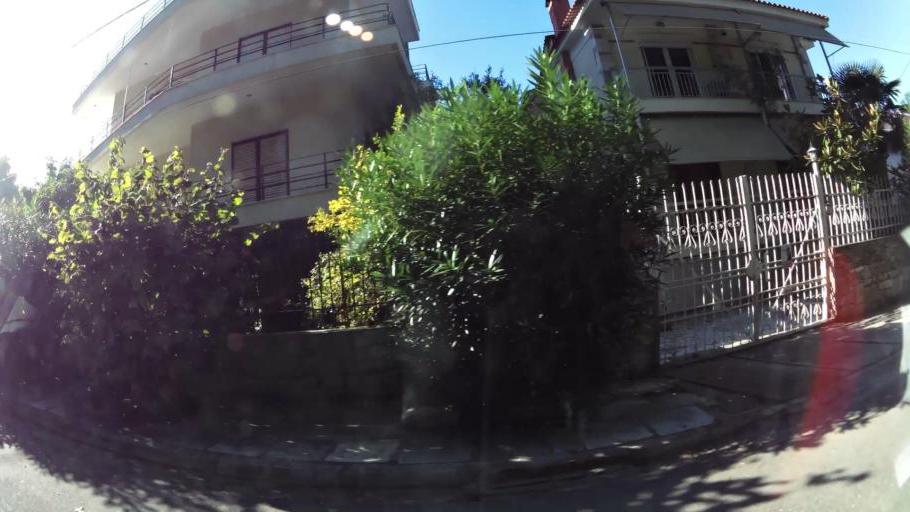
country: GR
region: Attica
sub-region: Nomarchia Anatolikis Attikis
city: Drosia
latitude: 38.1078
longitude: 23.8602
